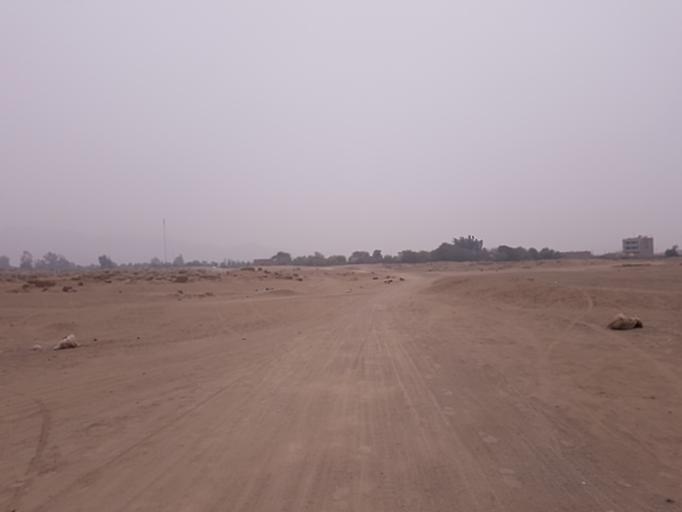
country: PE
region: Lima
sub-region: Lima
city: Santa Maria
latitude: -11.9840
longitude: -76.9154
